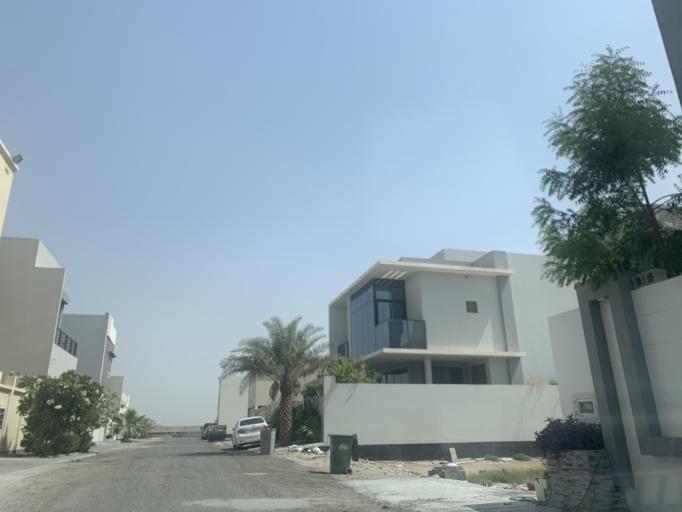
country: BH
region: Northern
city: Madinat `Isa
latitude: 26.1863
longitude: 50.4903
